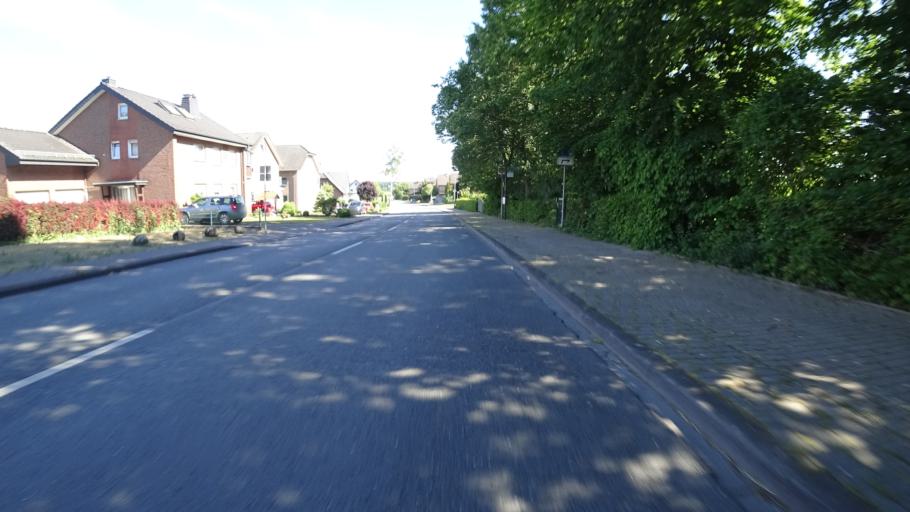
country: DE
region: North Rhine-Westphalia
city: Oelde
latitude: 51.8011
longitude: 8.2121
